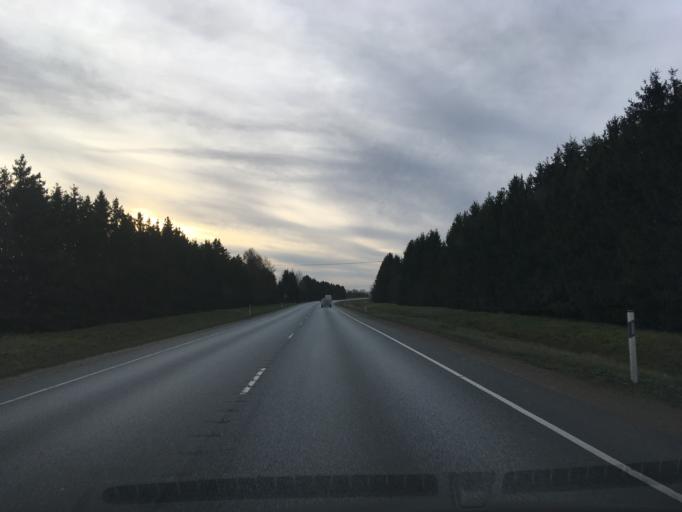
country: EE
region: Ida-Virumaa
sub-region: Kohtla-Nomme vald
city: Kohtla-Nomme
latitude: 59.4135
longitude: 27.1376
